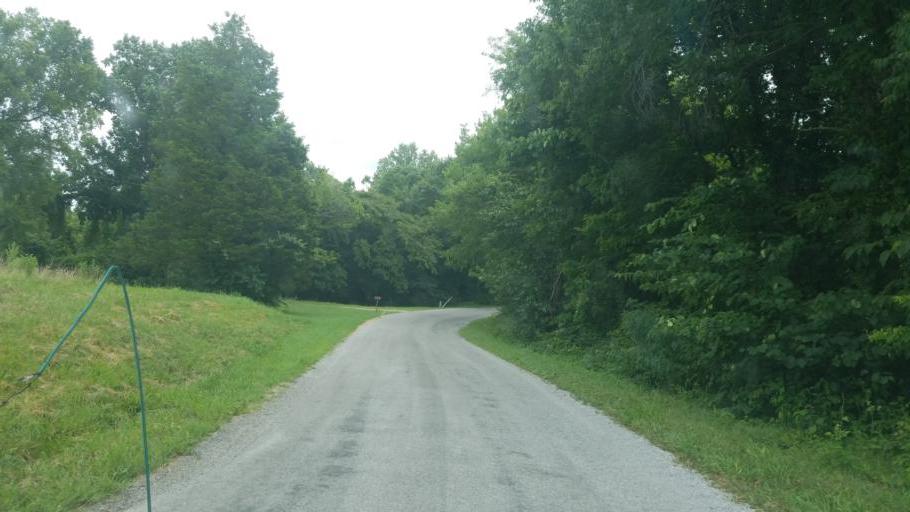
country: US
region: Illinois
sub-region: Jackson County
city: Murphysboro
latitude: 37.6880
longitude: -89.3876
